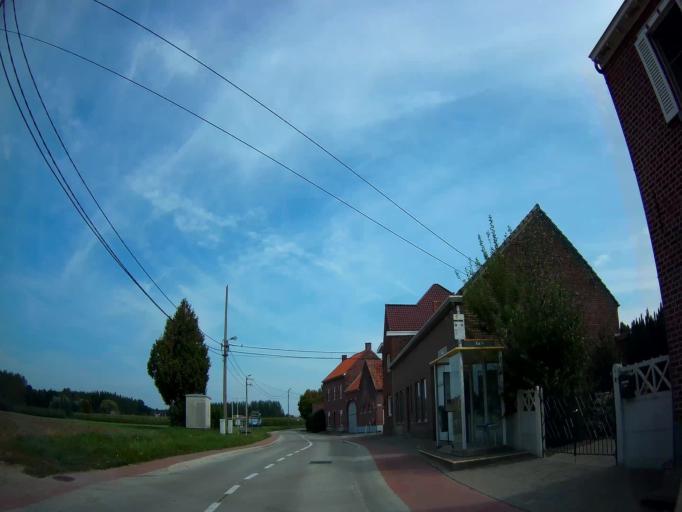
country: BE
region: Flanders
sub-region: Provincie Vlaams-Brabant
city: Zoutleeuw
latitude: 50.8268
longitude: 5.1258
